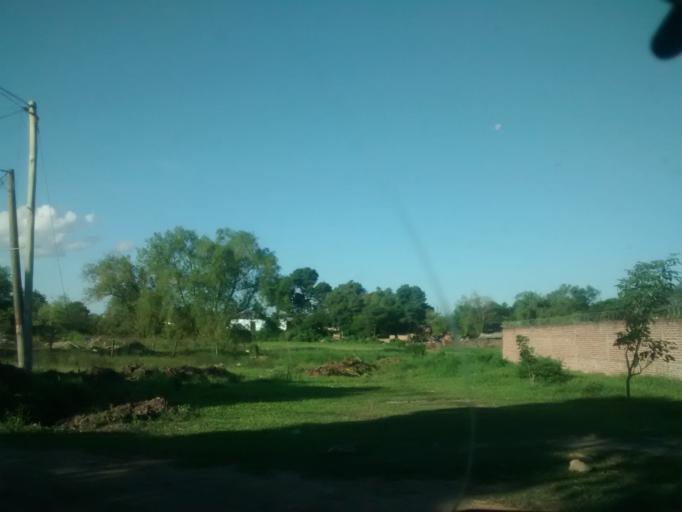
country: AR
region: Chaco
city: Resistencia
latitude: -27.4332
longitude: -58.9897
